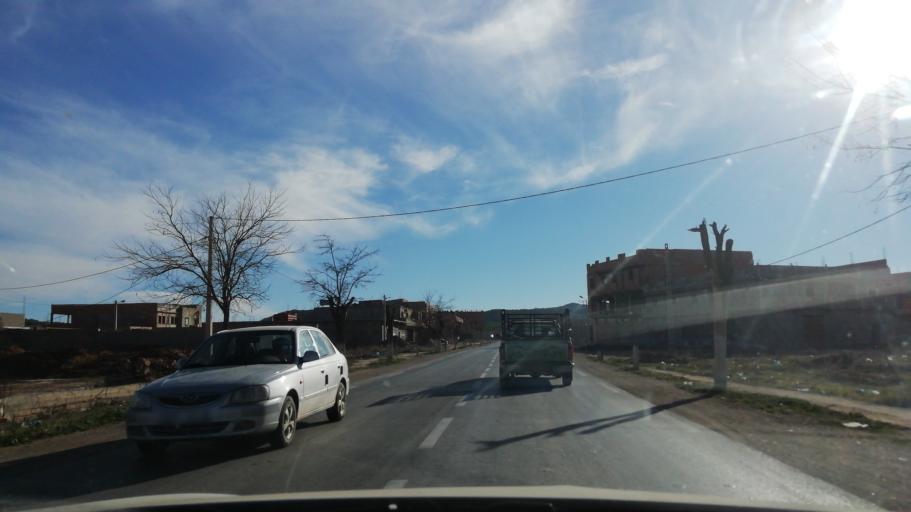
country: DZ
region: Tlemcen
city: Sebdou
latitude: 34.6246
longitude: -1.3340
